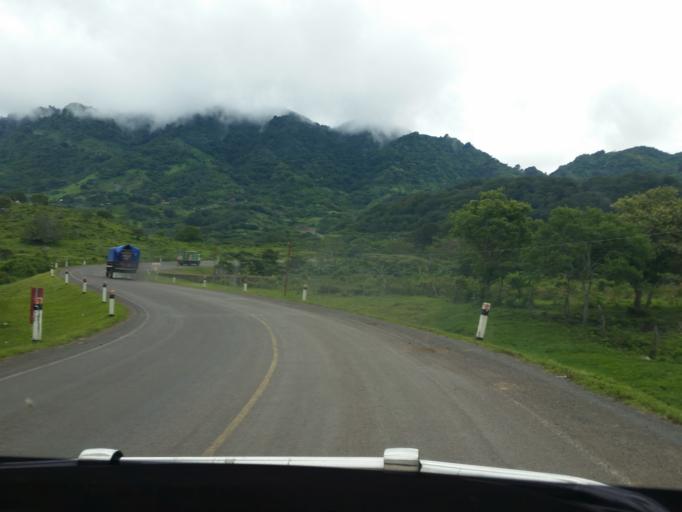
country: NI
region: Jinotega
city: Jinotega
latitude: 13.0618
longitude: -86.0007
